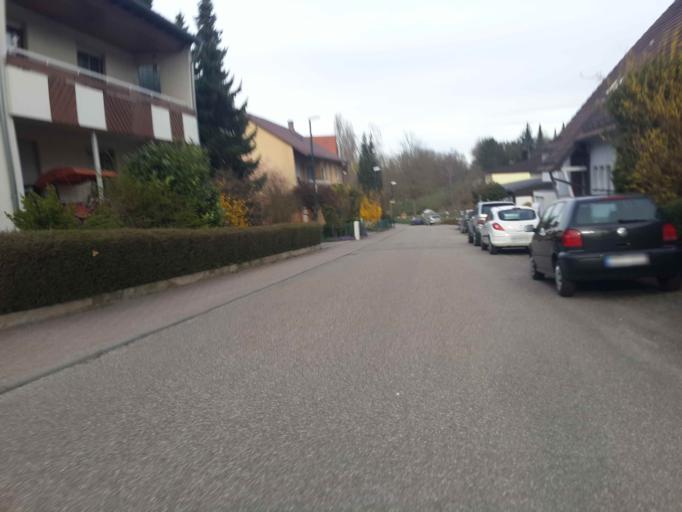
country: DE
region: Baden-Wuerttemberg
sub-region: Regierungsbezirk Stuttgart
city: Nordheim
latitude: 49.1065
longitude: 9.1368
